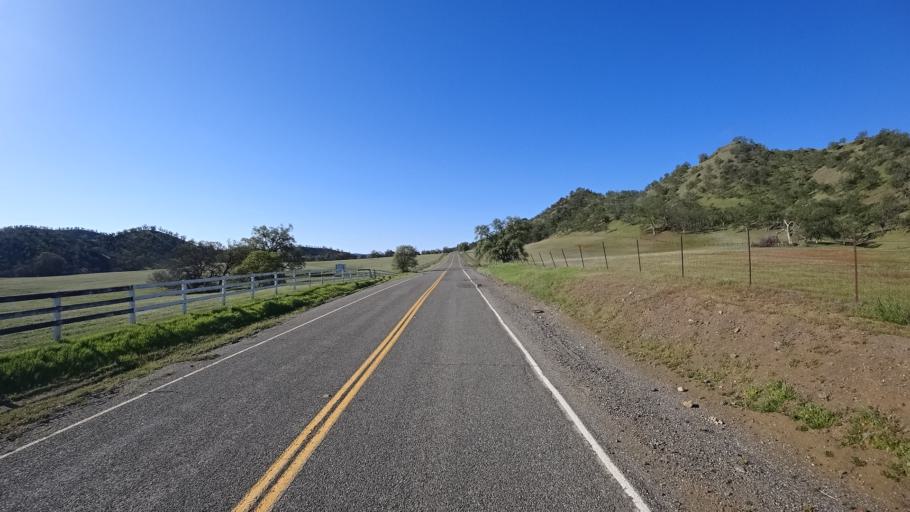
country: US
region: California
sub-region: Tehama County
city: Rancho Tehama Reserve
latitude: 39.7810
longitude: -122.5203
